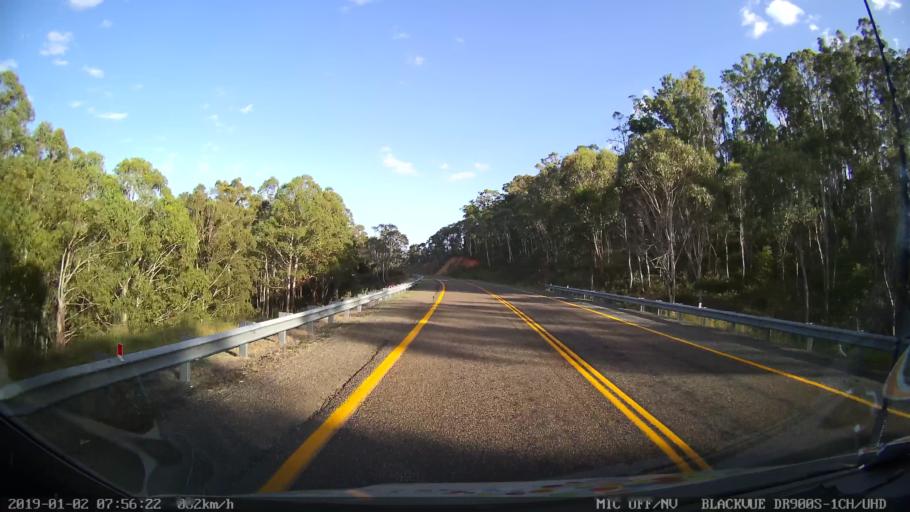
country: AU
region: New South Wales
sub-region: Tumut Shire
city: Tumut
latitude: -35.6715
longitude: 148.4856
